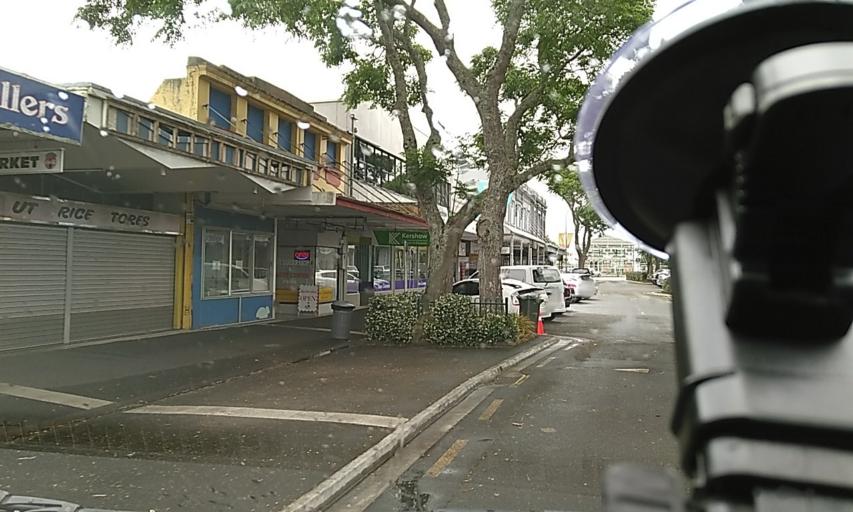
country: NZ
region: Waikato
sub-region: Hamilton City
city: Hamilton
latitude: -37.7882
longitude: 175.2645
